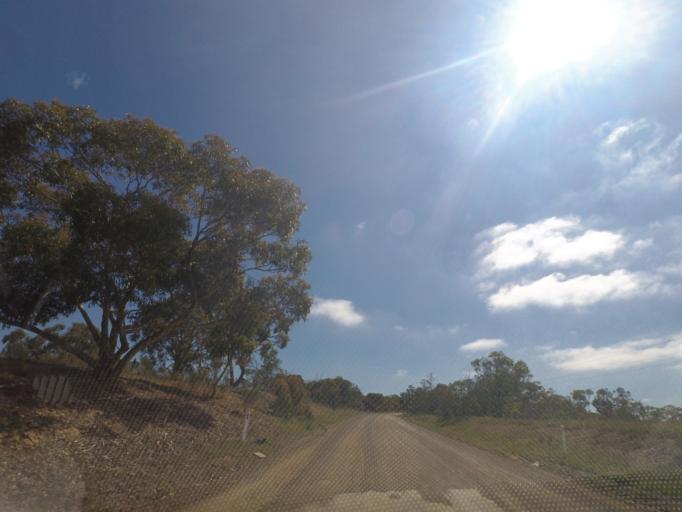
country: AU
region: Victoria
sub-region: Hume
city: Craigieburn
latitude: -37.4349
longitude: 144.9379
